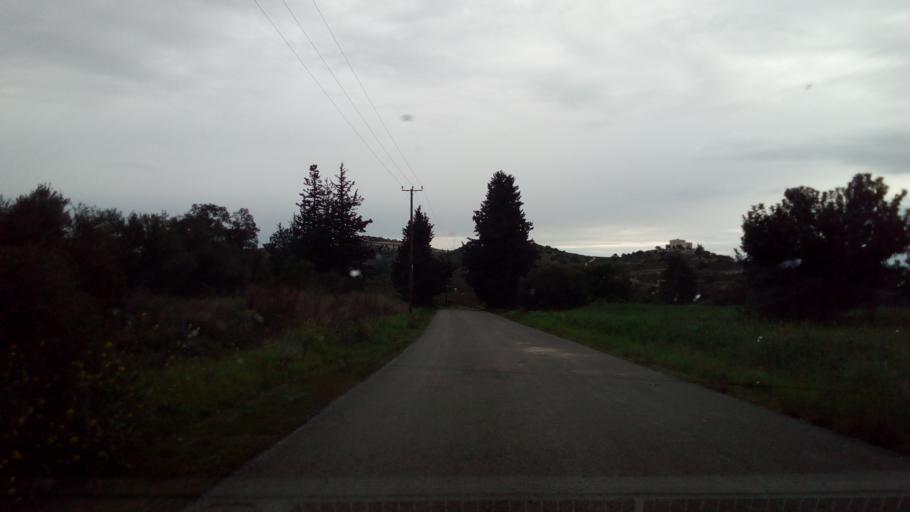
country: CY
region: Larnaka
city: Kofinou
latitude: 34.8576
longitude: 33.4489
